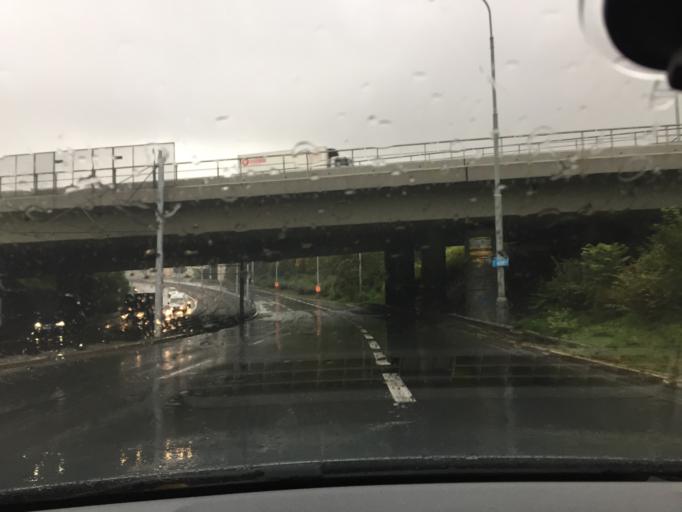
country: CZ
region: Praha
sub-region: Praha 8
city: Liben
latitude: 50.1172
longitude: 14.4675
